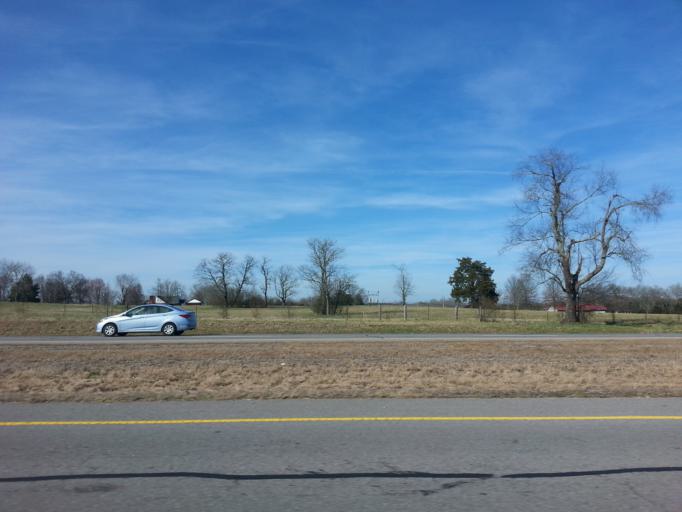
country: US
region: Tennessee
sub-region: Rutherford County
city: Murfreesboro
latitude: 35.8275
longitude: -86.2952
